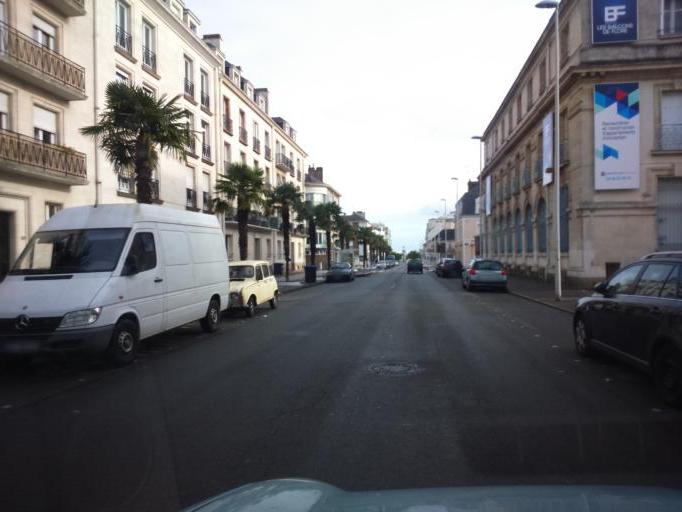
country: FR
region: Pays de la Loire
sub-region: Departement de la Loire-Atlantique
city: Saint-Nazaire
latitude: 47.2737
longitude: -2.2090
